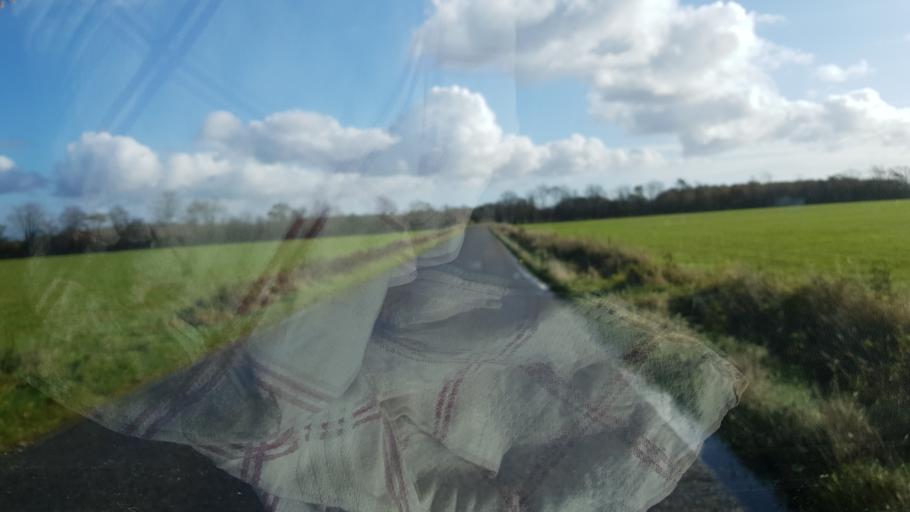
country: DK
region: South Denmark
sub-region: Varde Kommune
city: Olgod
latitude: 55.6917
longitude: 8.6525
